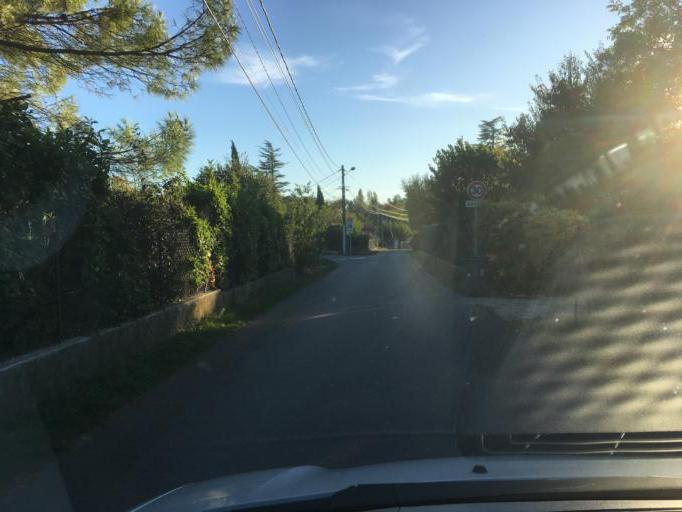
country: FR
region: Provence-Alpes-Cote d'Azur
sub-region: Departement du Vaucluse
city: Mazan
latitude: 44.0567
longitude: 5.1130
